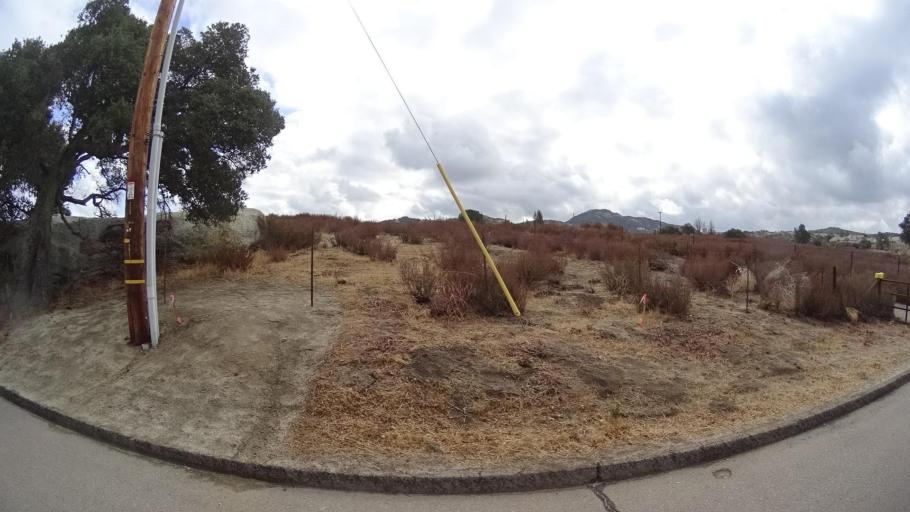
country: US
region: California
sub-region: San Diego County
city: Campo
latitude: 32.6230
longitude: -116.4632
